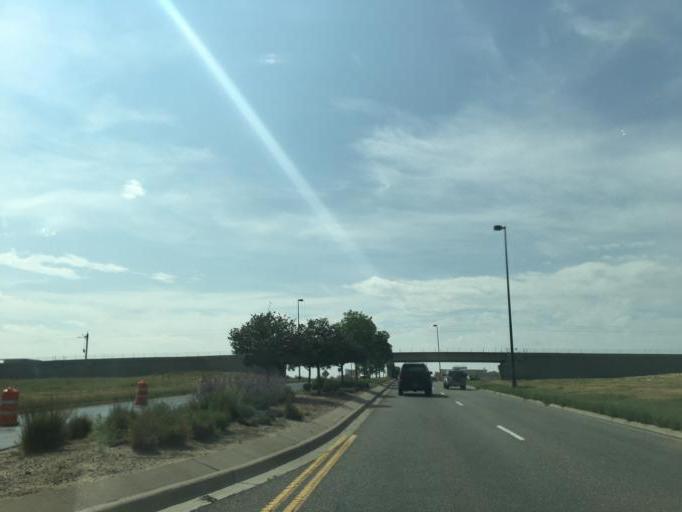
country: US
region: Colorado
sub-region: Adams County
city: Aurora
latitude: 39.8295
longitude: -104.7720
